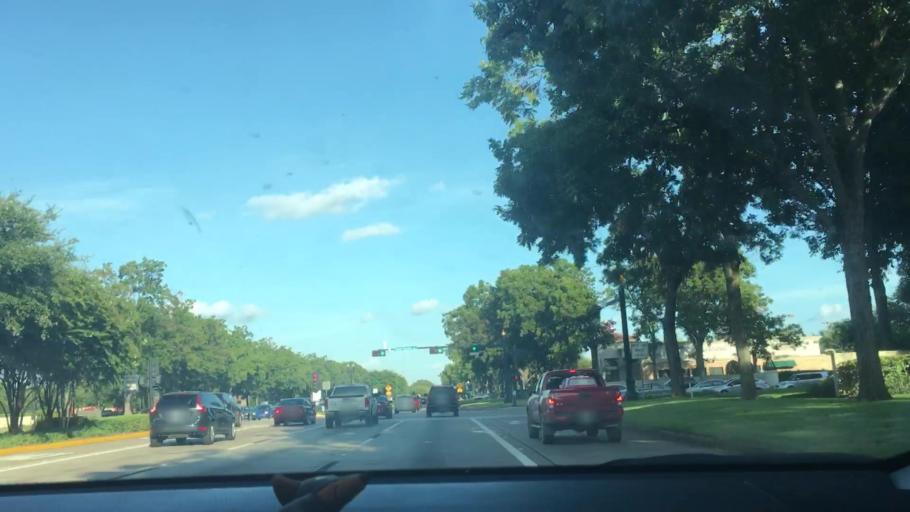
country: US
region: Texas
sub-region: Fort Bend County
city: Sugar Land
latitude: 29.5973
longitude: -95.6199
